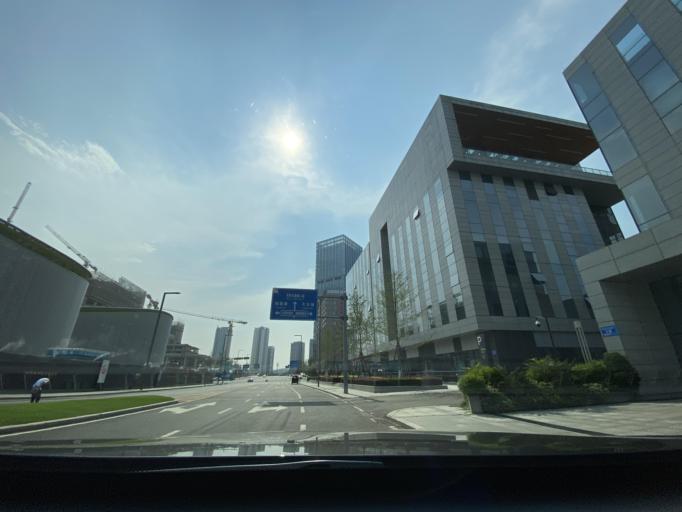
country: CN
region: Sichuan
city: Dongsheng
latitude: 30.3958
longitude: 104.0745
